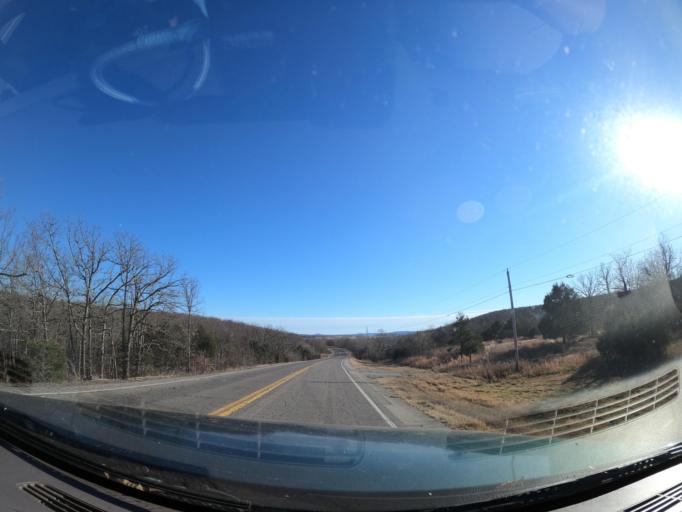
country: US
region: Oklahoma
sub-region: Pittsburg County
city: Longtown
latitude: 35.2217
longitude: -95.4294
